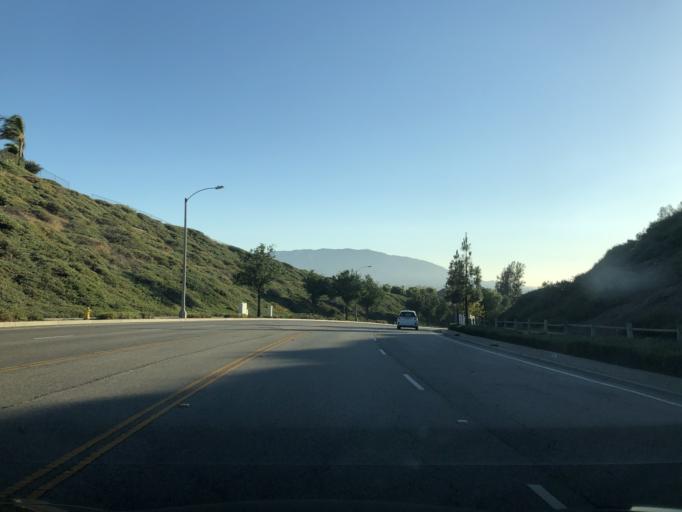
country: US
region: California
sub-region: Riverside County
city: Corona
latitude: 33.8967
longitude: -117.5487
